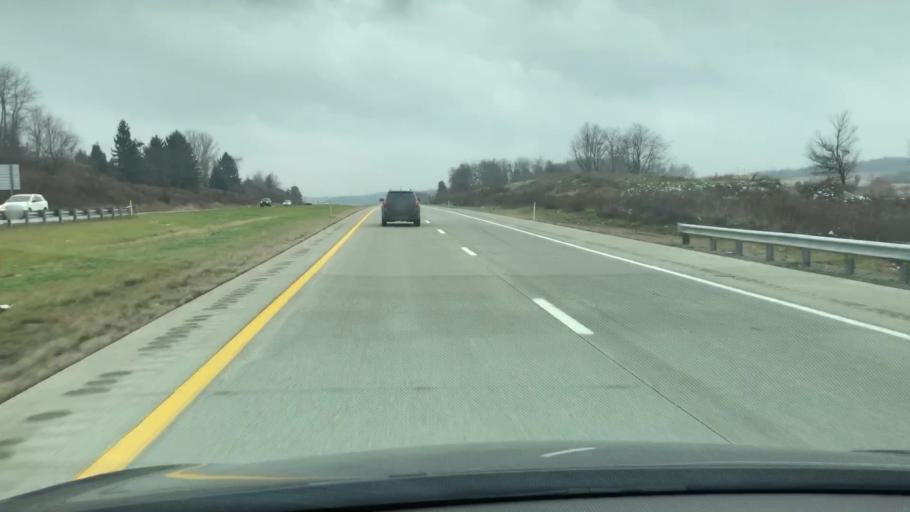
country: US
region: Pennsylvania
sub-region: Westmoreland County
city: Mount Pleasant
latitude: 40.1700
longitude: -79.5602
